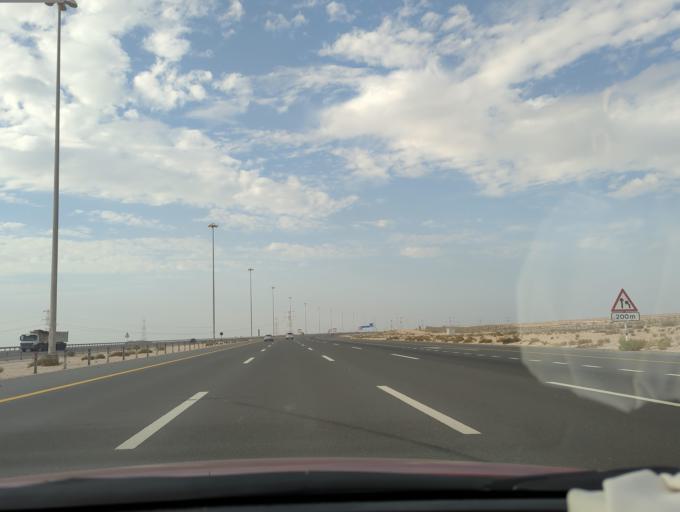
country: AE
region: Abu Dhabi
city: Abu Dhabi
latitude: 24.4453
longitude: 54.7557
